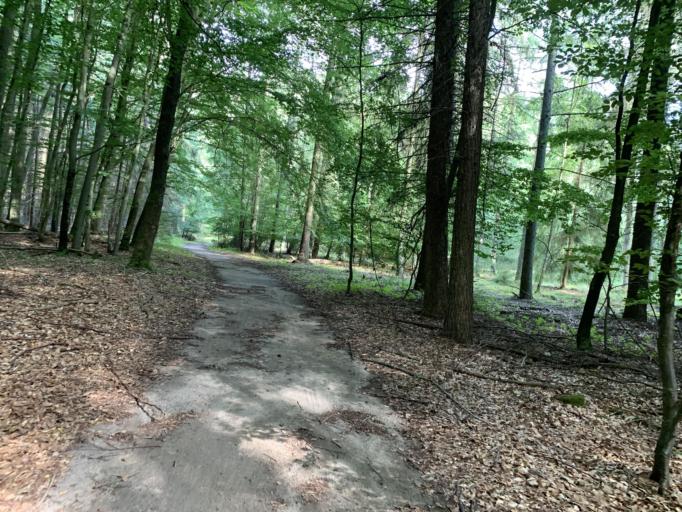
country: DE
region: Mecklenburg-Vorpommern
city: Carpin
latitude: 53.3493
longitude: 13.2255
